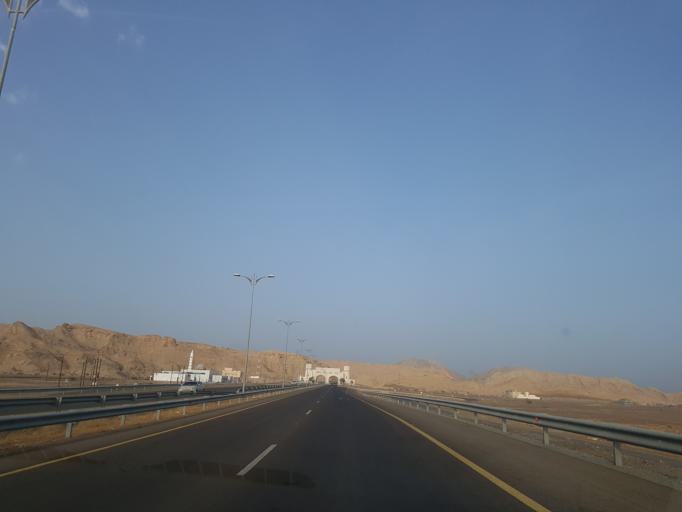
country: OM
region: Al Buraimi
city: Al Buraymi
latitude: 24.2317
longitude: 55.9292
